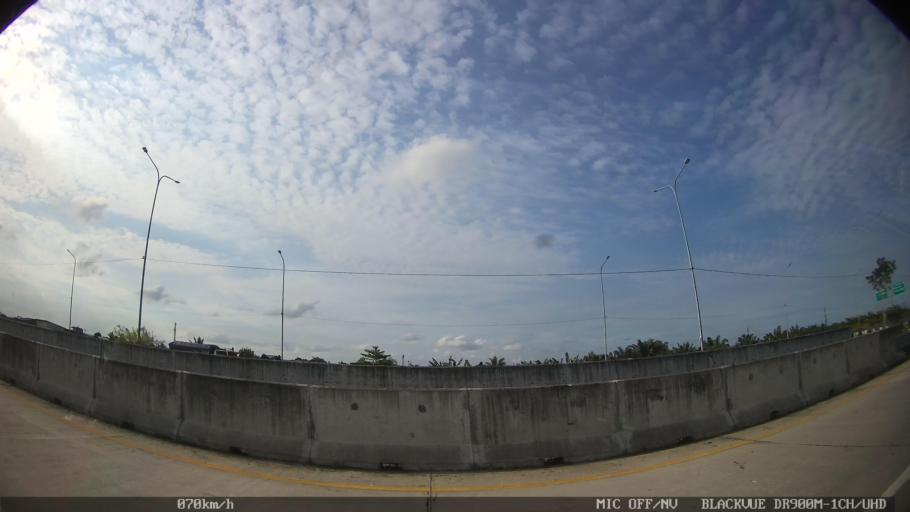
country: ID
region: North Sumatra
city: Medan
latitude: 3.6482
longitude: 98.6775
